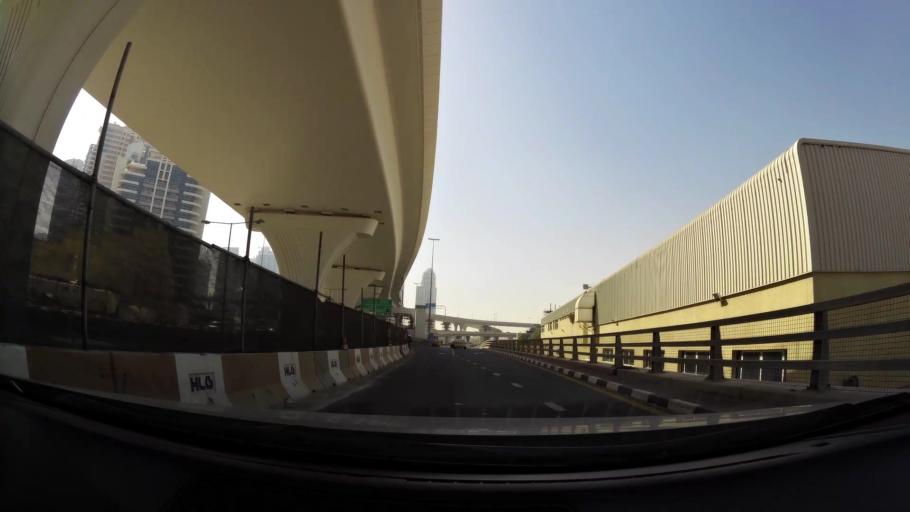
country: AE
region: Dubai
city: Dubai
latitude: 25.0674
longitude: 55.1292
